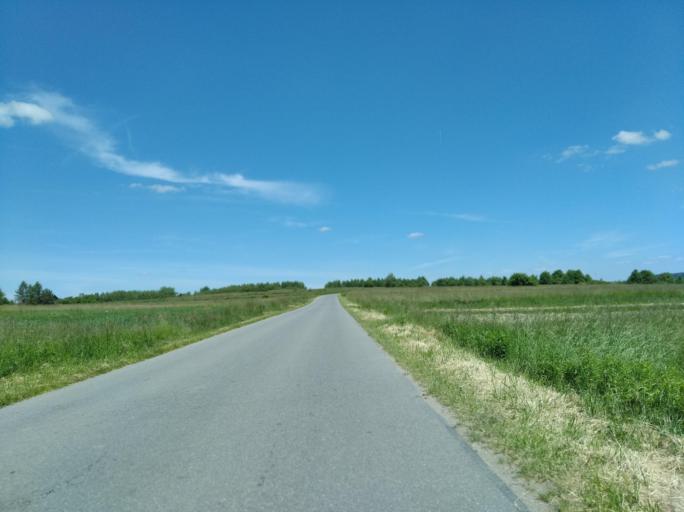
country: PL
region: Subcarpathian Voivodeship
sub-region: Powiat jasielski
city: Osiek Jasielski
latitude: 49.6569
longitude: 21.5307
